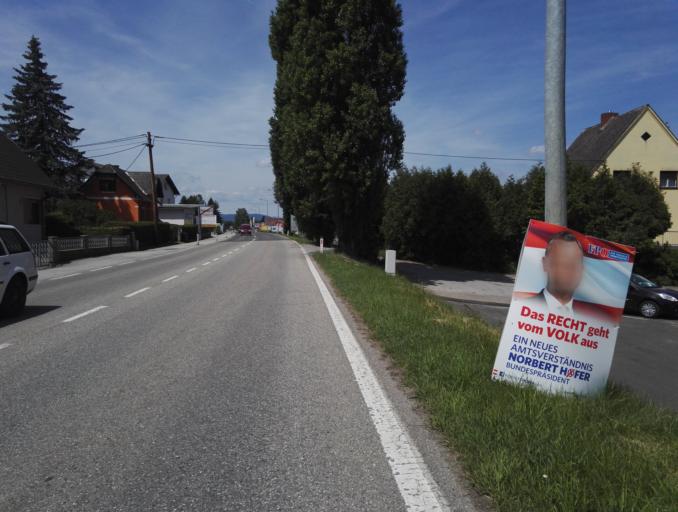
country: AT
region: Styria
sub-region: Politischer Bezirk Graz-Umgebung
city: Kalsdorf bei Graz
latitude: 46.9751
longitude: 15.4705
